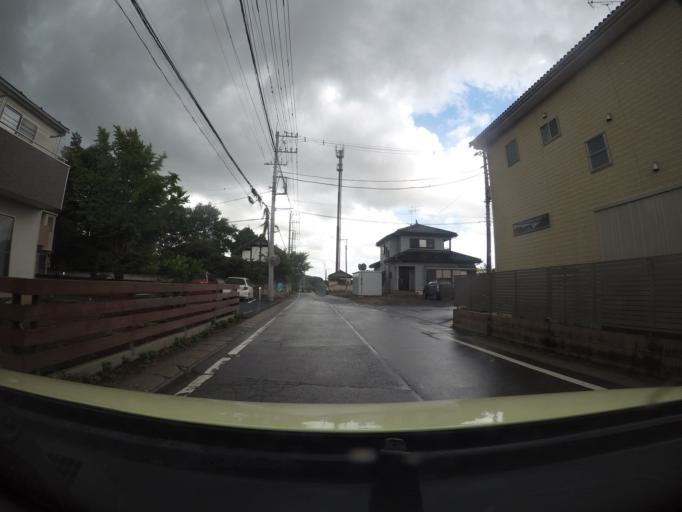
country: JP
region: Ibaraki
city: Iwai
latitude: 36.0434
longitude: 139.8999
